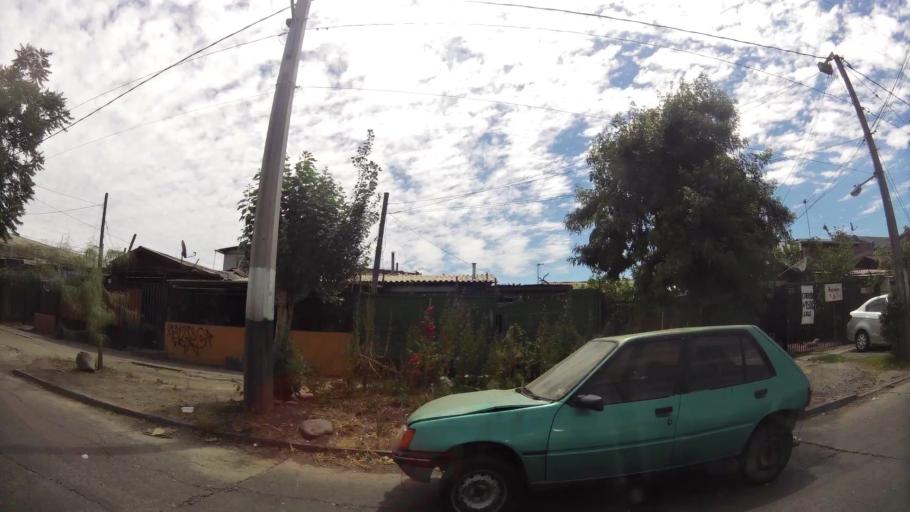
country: CL
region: Santiago Metropolitan
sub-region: Provincia de Santiago
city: La Pintana
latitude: -33.5747
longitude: -70.6574
